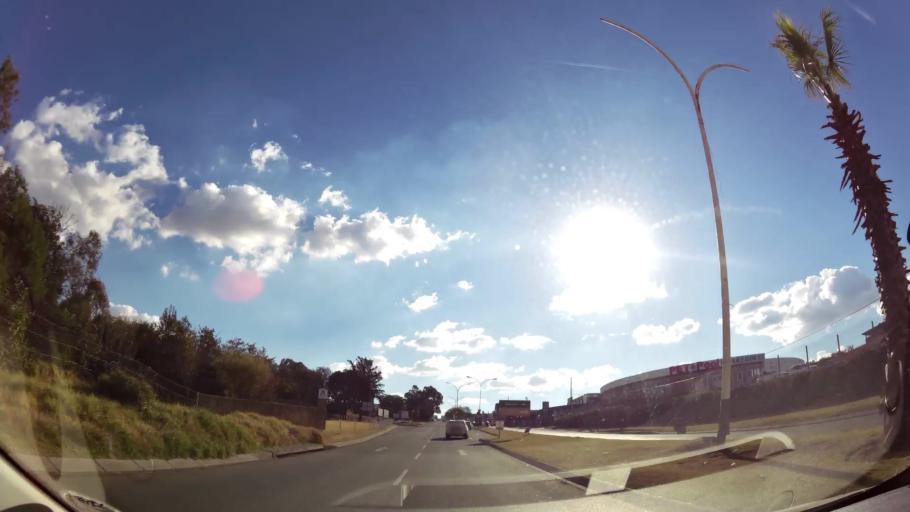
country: ZA
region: Mpumalanga
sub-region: Nkangala District Municipality
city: Witbank
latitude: -25.8775
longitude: 29.2460
